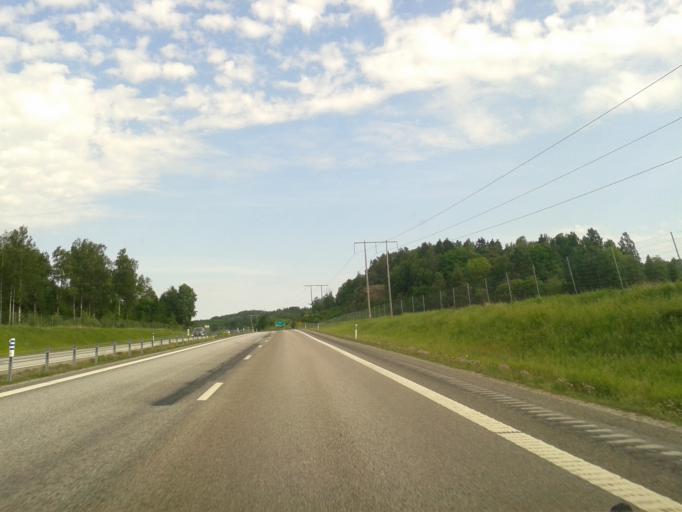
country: SE
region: Vaestra Goetaland
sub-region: Munkedals Kommun
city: Munkedal
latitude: 58.5236
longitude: 11.5467
